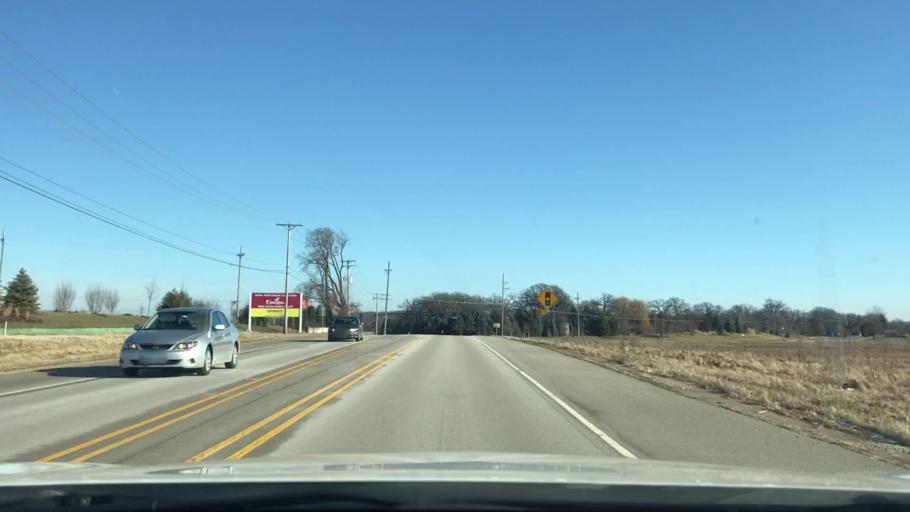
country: US
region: Illinois
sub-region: Kane County
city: Pingree Grove
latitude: 42.0886
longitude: -88.4314
